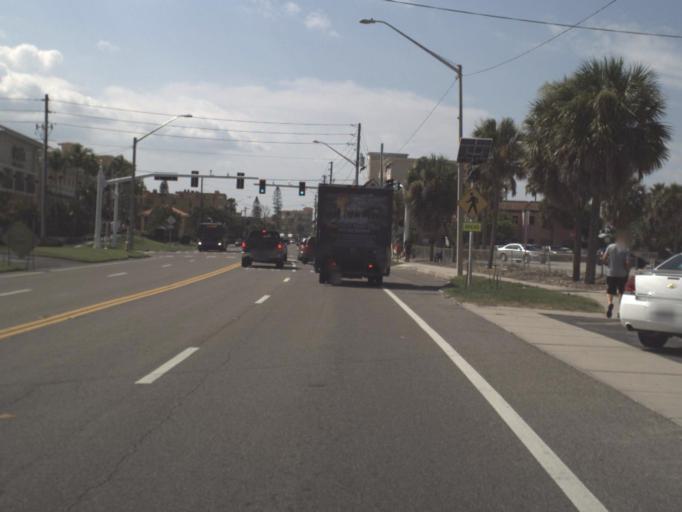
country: US
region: Florida
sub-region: Pinellas County
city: Treasure Island
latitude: 27.7669
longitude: -82.7686
